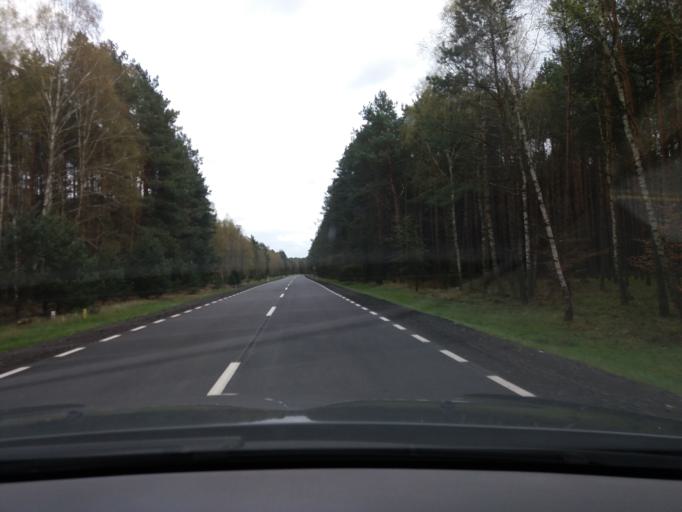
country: PL
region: Lubusz
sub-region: Powiat sulecinski
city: Lubniewice
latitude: 52.5868
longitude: 15.2312
